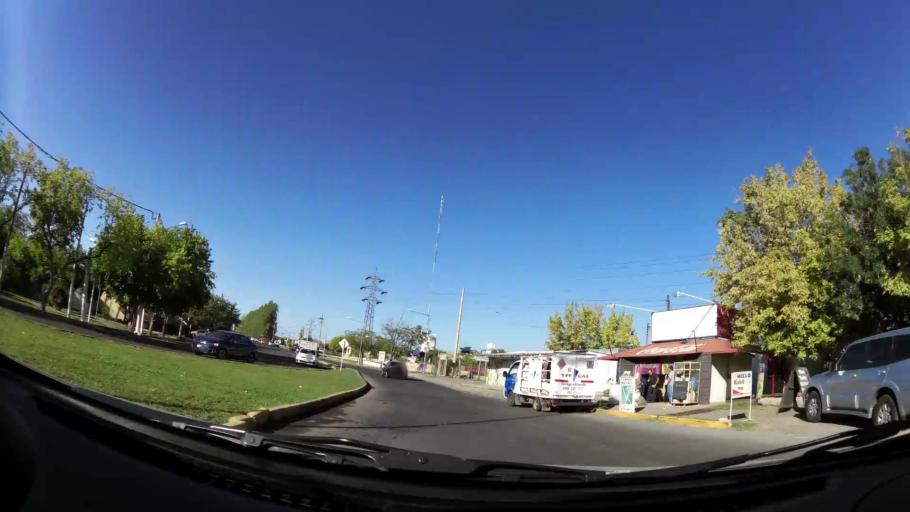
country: AR
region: Mendoza
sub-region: Departamento de Godoy Cruz
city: Godoy Cruz
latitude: -32.9291
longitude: -68.8386
